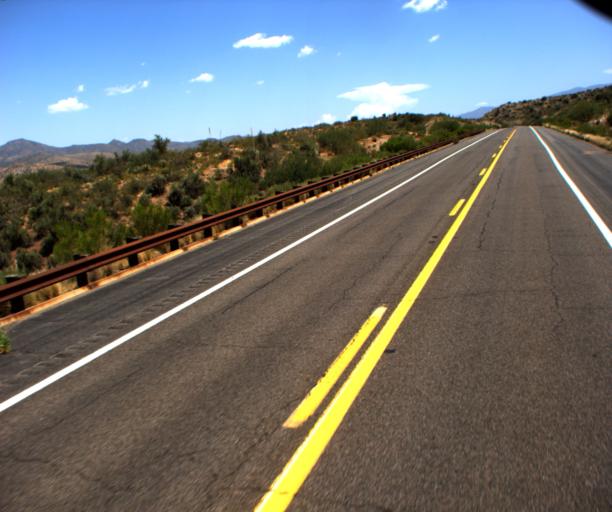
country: US
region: Arizona
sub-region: Gila County
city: Claypool
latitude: 33.5015
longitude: -110.8675
